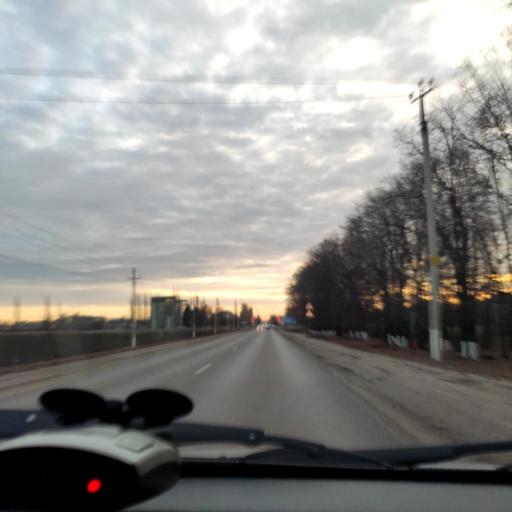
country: RU
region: Voronezj
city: Ramon'
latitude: 51.9201
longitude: 39.2889
